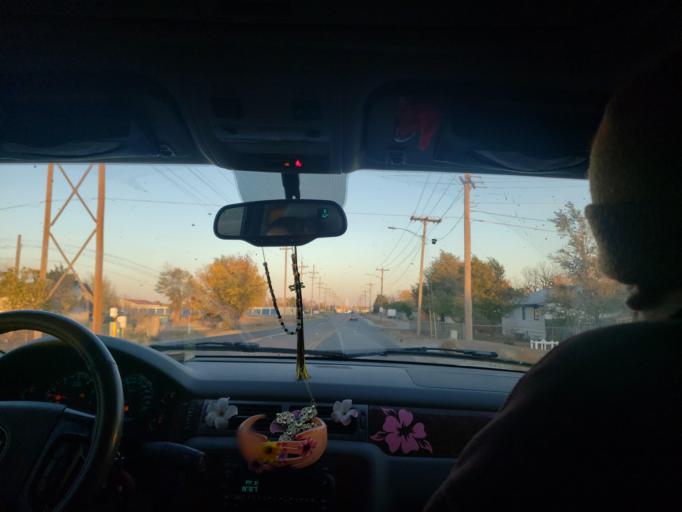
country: US
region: Kansas
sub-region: Finney County
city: Garden City
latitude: 37.9895
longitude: -100.8928
